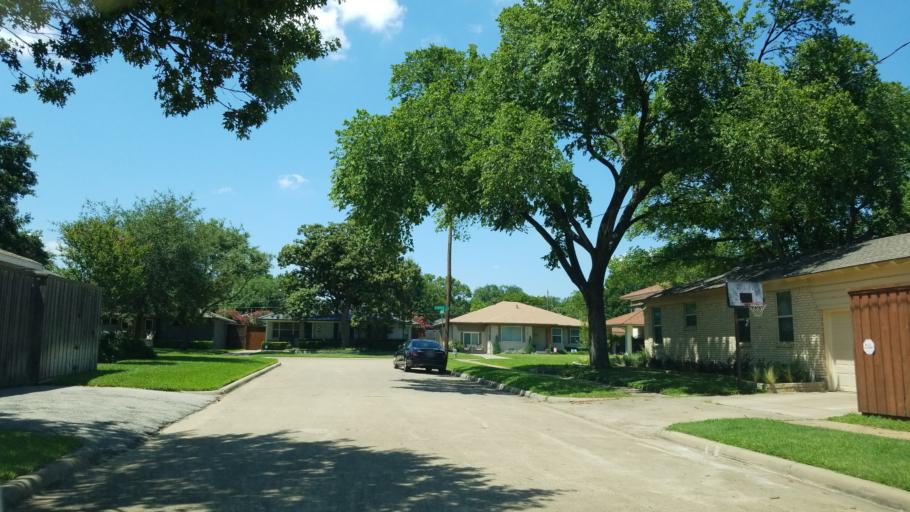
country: US
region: Texas
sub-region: Dallas County
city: University Park
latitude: 32.8722
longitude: -96.8418
